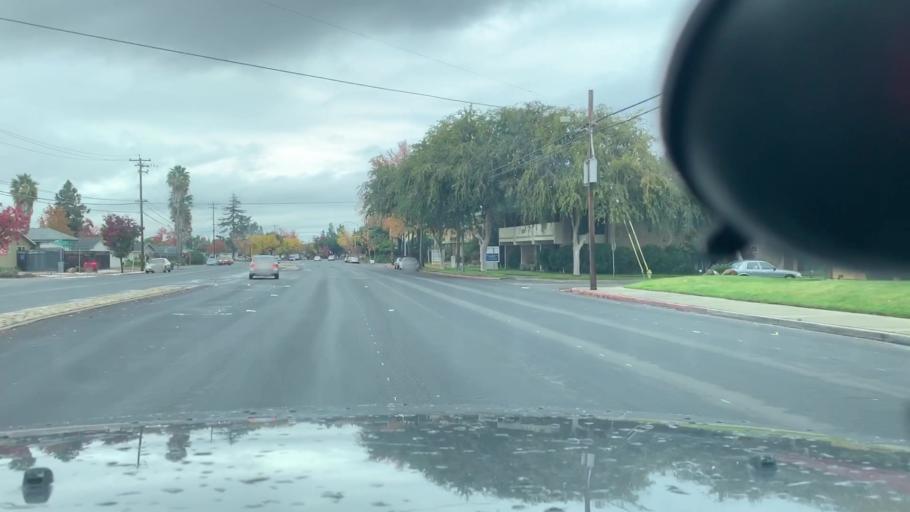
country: US
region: California
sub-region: Santa Clara County
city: Campbell
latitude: 37.3103
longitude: -121.9773
